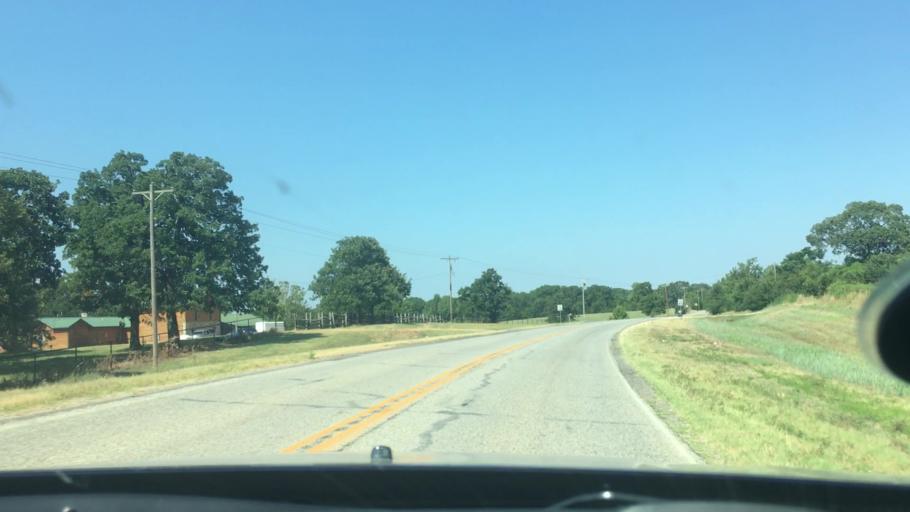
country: US
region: Oklahoma
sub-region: Johnston County
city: Tishomingo
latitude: 34.2379
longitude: -96.5604
